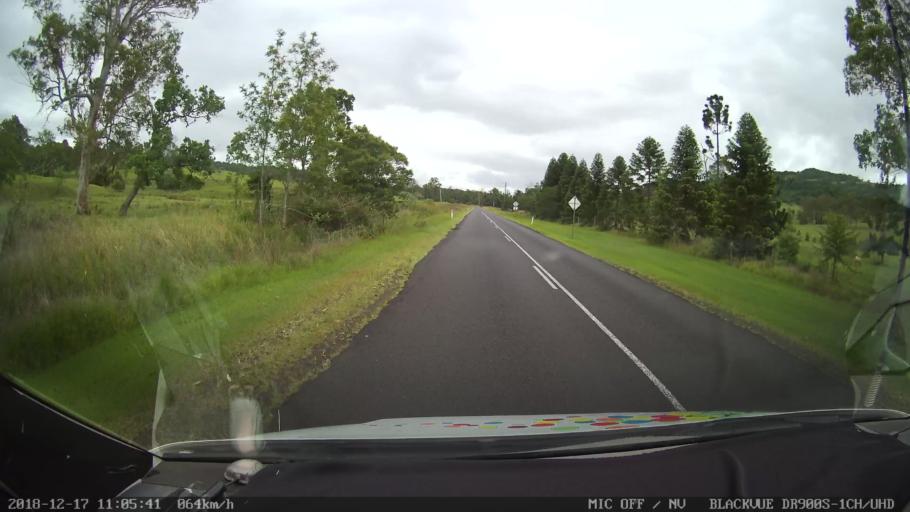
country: AU
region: New South Wales
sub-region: Kyogle
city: Kyogle
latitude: -28.7881
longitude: 152.6479
